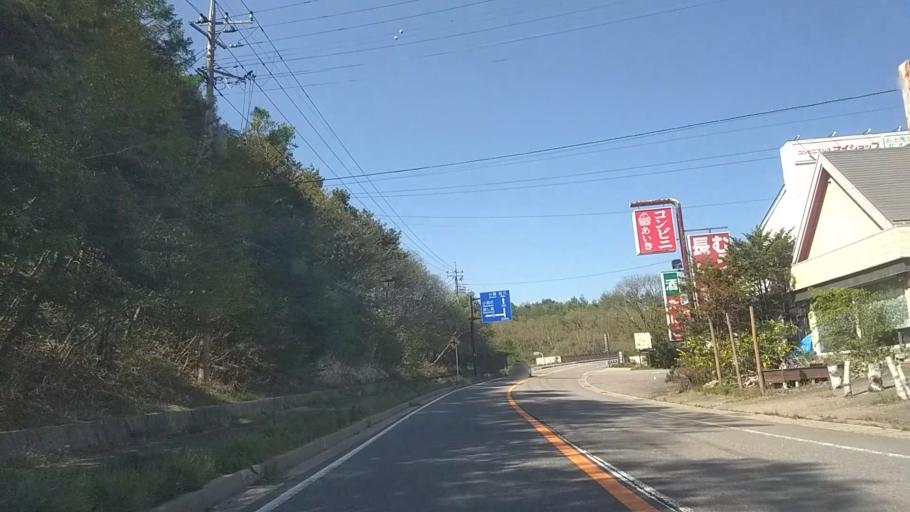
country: JP
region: Yamanashi
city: Nirasaki
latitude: 35.9290
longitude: 138.4429
